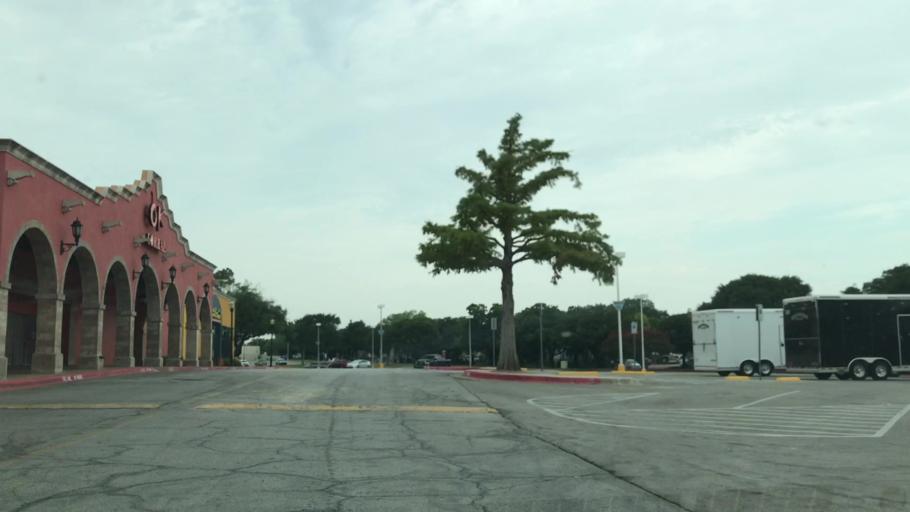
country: US
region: Texas
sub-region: Tarrant County
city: Edgecliff Village
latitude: 32.6879
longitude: -97.3235
